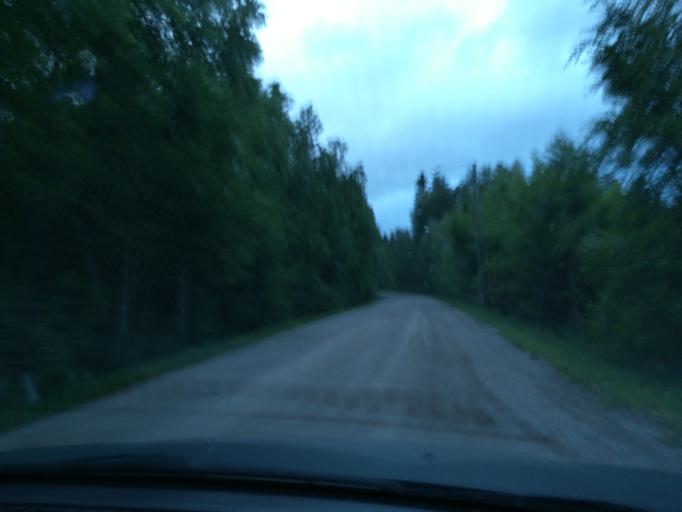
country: FI
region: Southern Savonia
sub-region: Mikkeli
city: Ristiina
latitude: 61.4910
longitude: 27.2784
